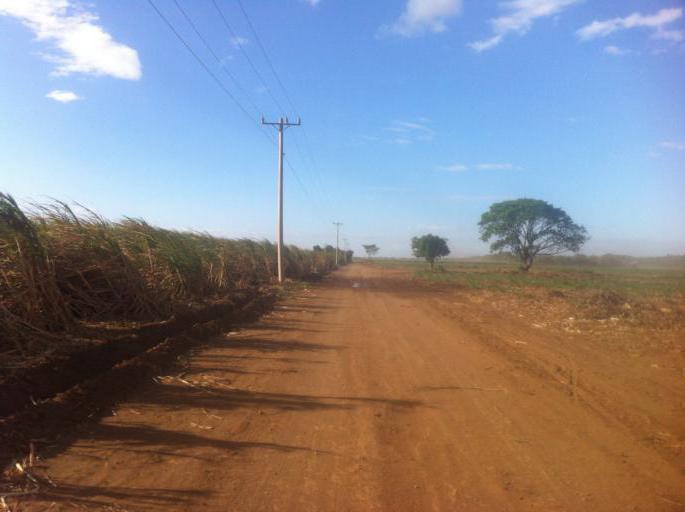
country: NI
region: Managua
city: Masachapa
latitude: 11.8566
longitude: -86.5507
